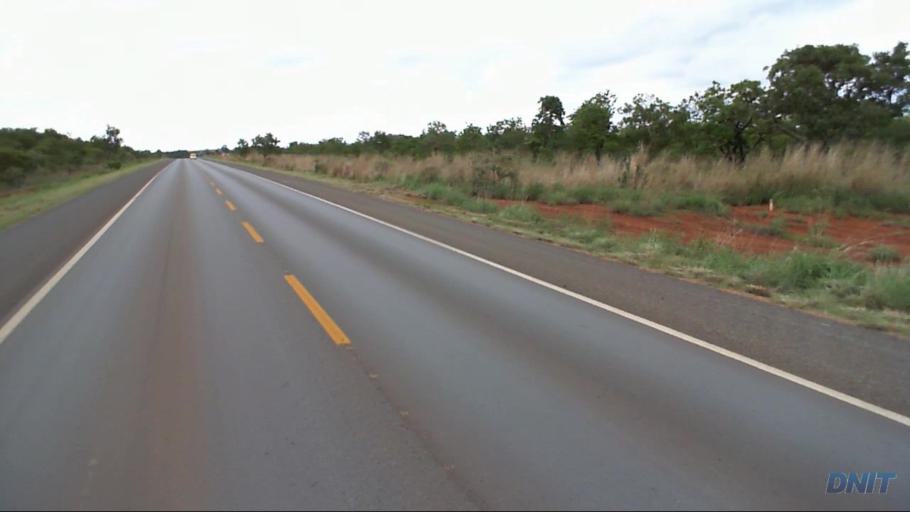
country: BR
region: Goias
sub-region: Barro Alto
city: Barro Alto
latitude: -15.2091
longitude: -48.6858
